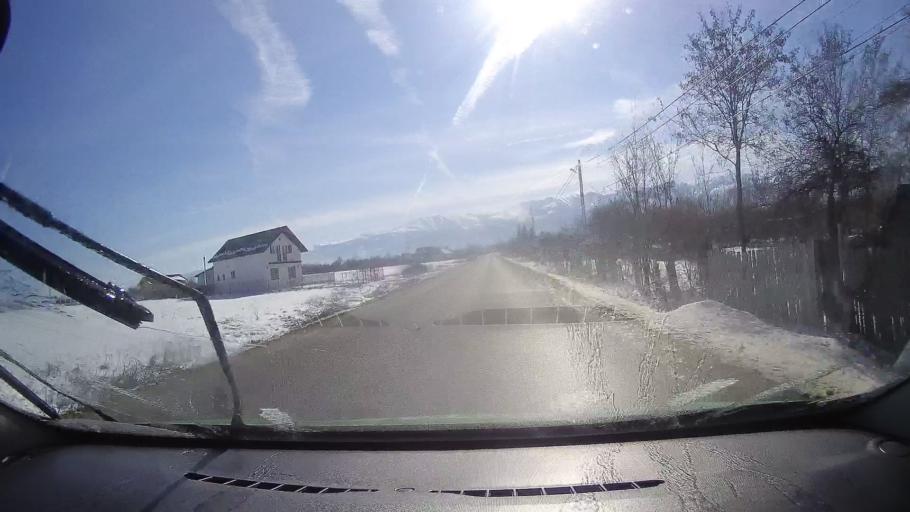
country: RO
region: Brasov
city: Ucea de Sus
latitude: 45.7531
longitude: 24.6911
